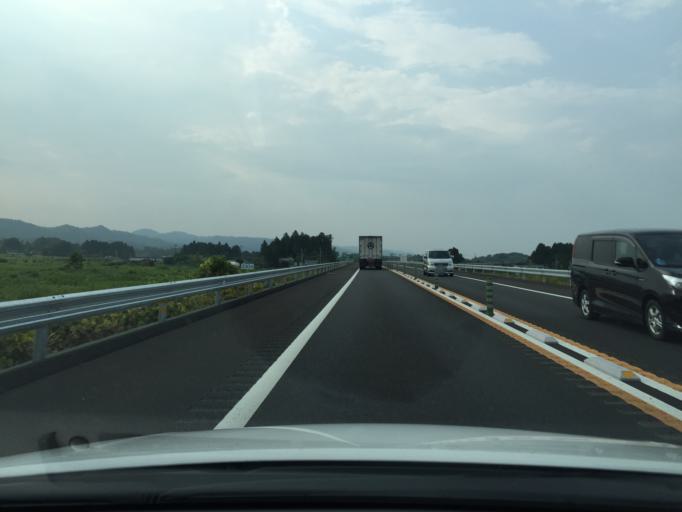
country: JP
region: Fukushima
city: Namie
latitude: 37.4814
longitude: 140.9559
